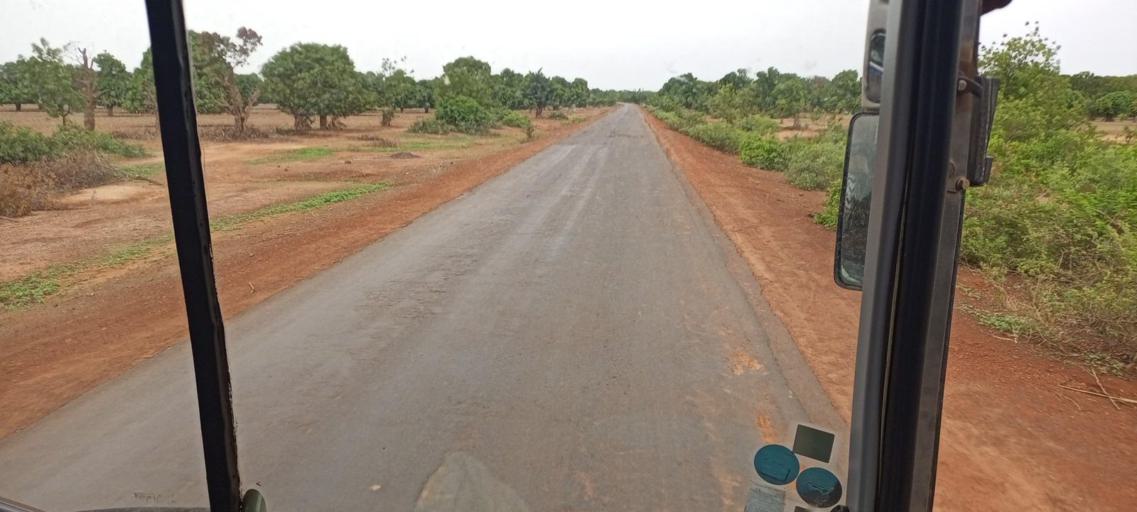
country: ML
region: Segou
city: Bla
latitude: 12.6835
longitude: -5.7236
